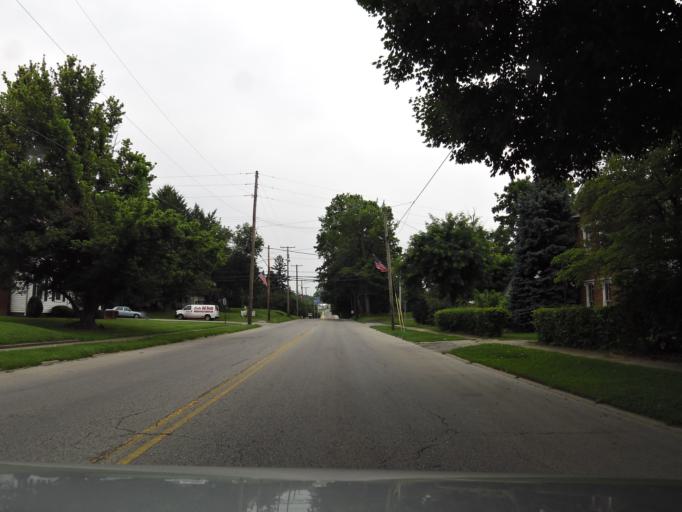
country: US
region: Ohio
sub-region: Clinton County
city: Wilmington
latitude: 39.4393
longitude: -83.8292
